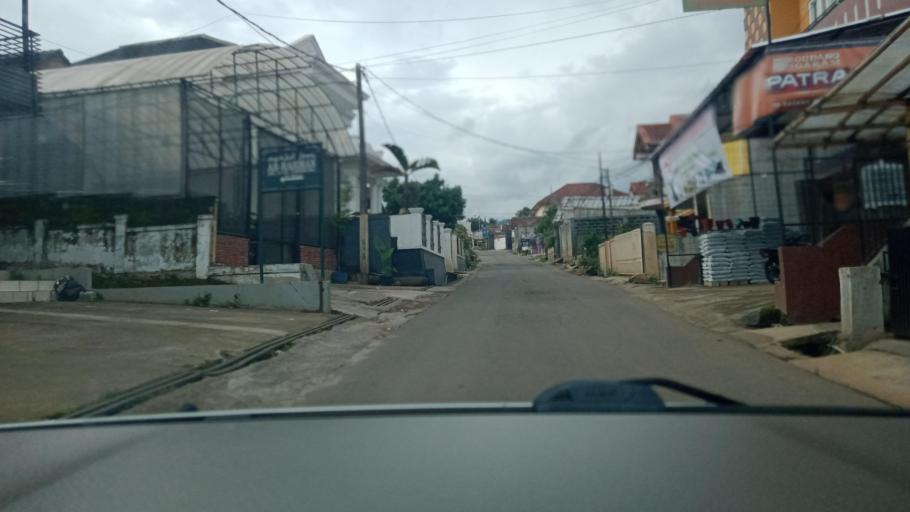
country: ID
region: West Java
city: Lembang
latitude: -6.8113
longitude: 107.5932
